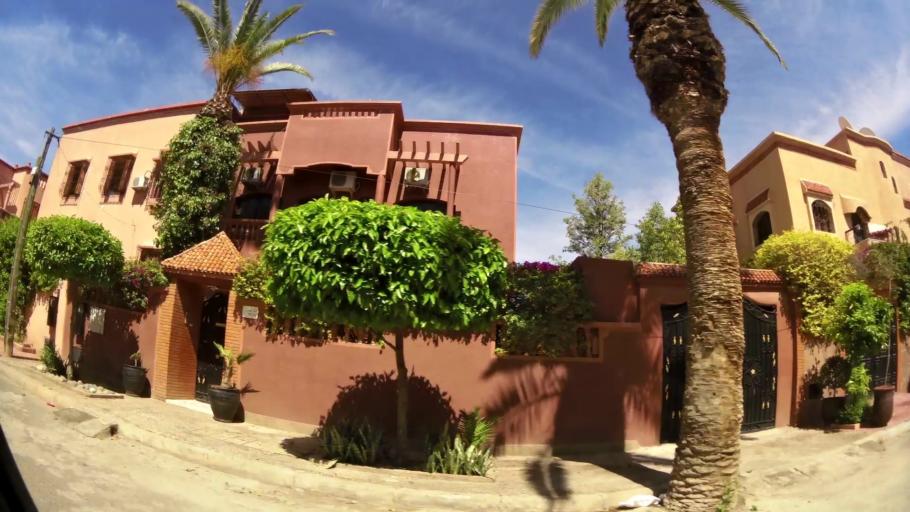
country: MA
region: Marrakech-Tensift-Al Haouz
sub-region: Marrakech
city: Marrakesh
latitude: 31.6640
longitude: -7.9919
